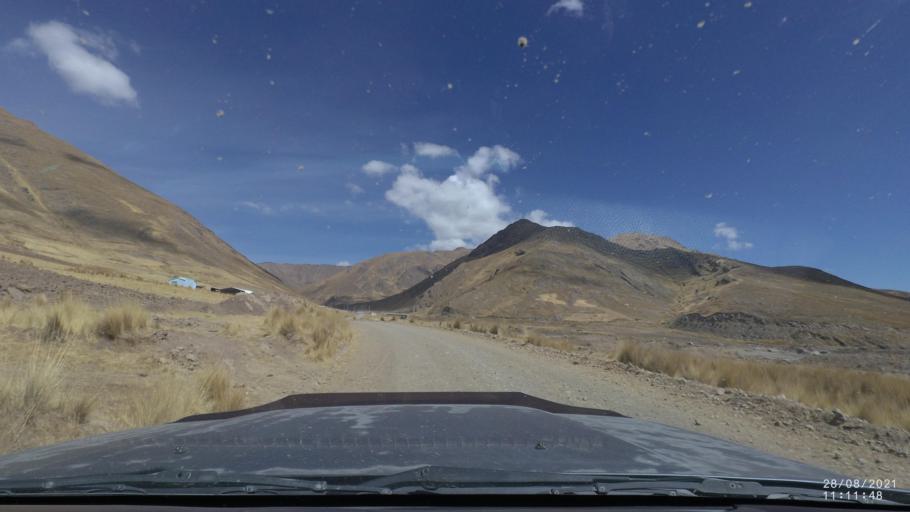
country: BO
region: Cochabamba
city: Cochabamba
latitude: -17.1486
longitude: -66.3146
